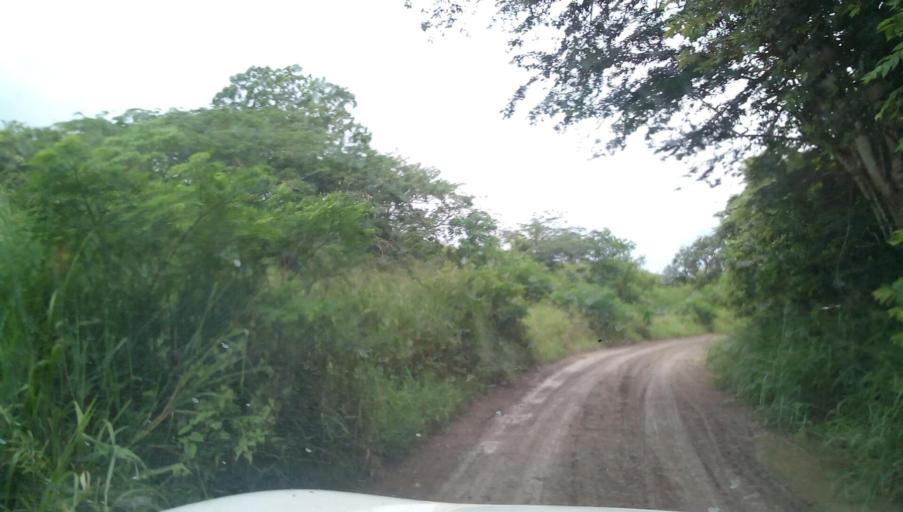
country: MX
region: Veracruz
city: Panuco
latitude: 21.8097
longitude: -98.1098
